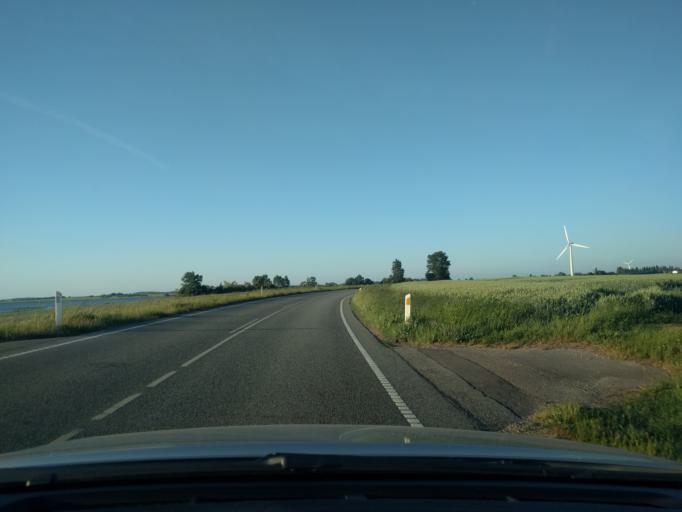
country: DK
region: South Denmark
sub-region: Kerteminde Kommune
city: Kerteminde
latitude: 55.4827
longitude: 10.6191
